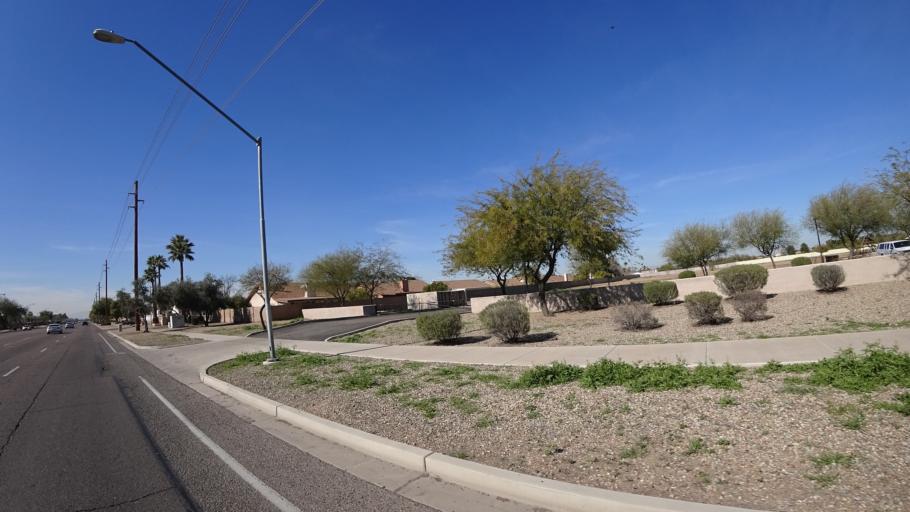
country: US
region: Arizona
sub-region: Maricopa County
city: Tolleson
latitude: 33.5089
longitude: -112.2414
